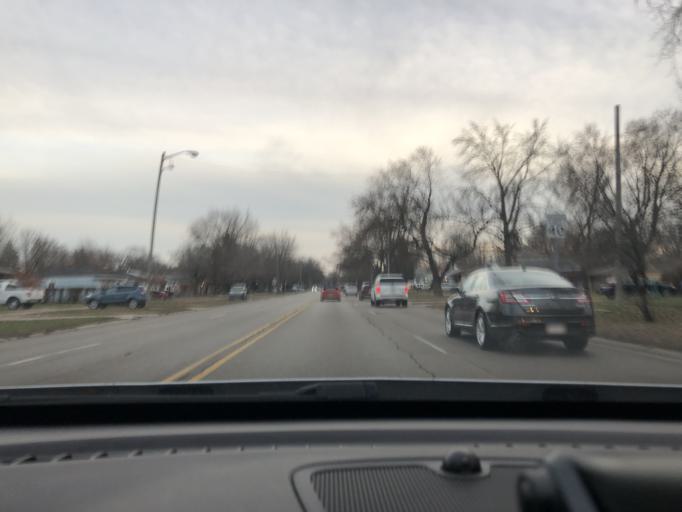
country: US
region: Michigan
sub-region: Wayne County
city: Allen Park
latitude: 42.2769
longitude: -83.2314
